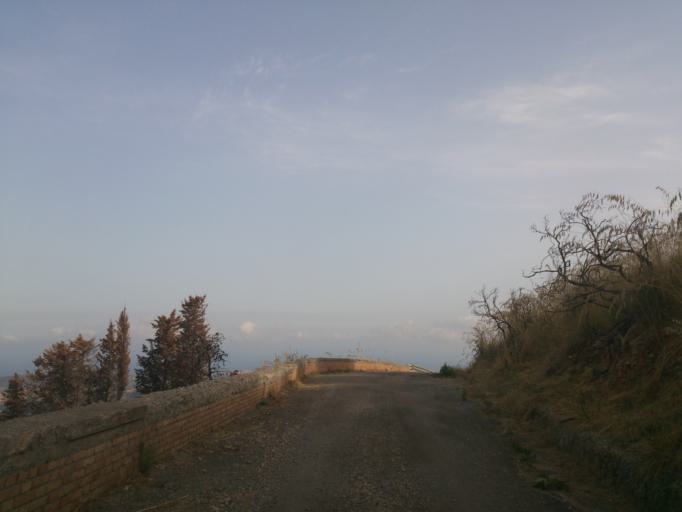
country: IT
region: Calabria
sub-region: Provincia di Reggio Calabria
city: Pazzano
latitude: 38.4702
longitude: 16.4506
